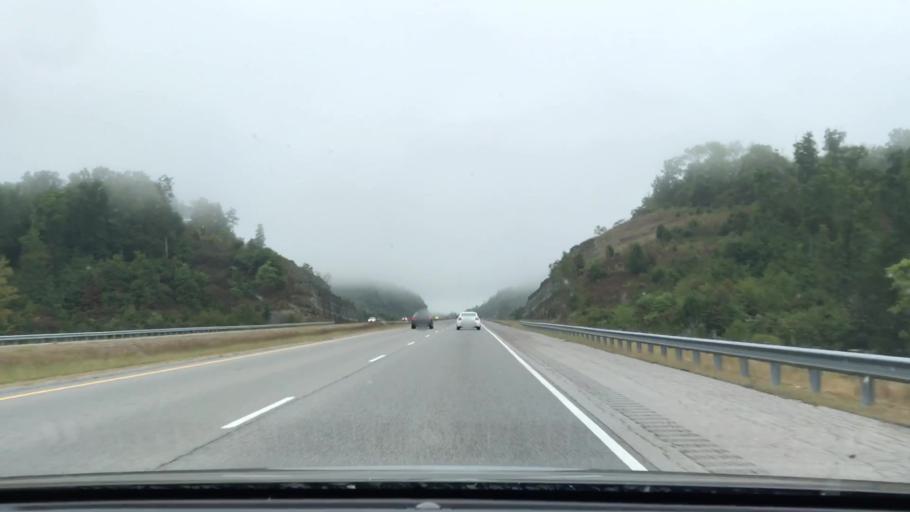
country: US
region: Tennessee
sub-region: Sumner County
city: Gallatin
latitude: 36.4601
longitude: -86.4681
